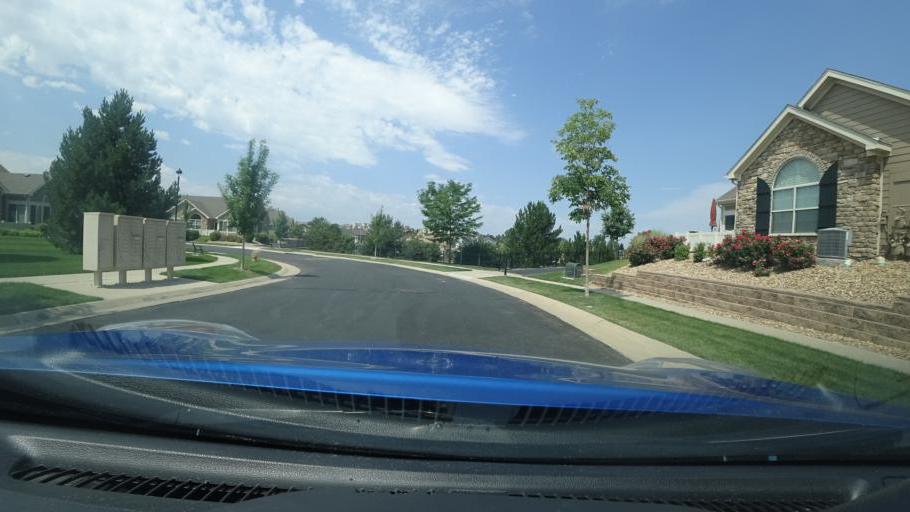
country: US
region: Colorado
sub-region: Adams County
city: Aurora
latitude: 39.6813
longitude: -104.7617
